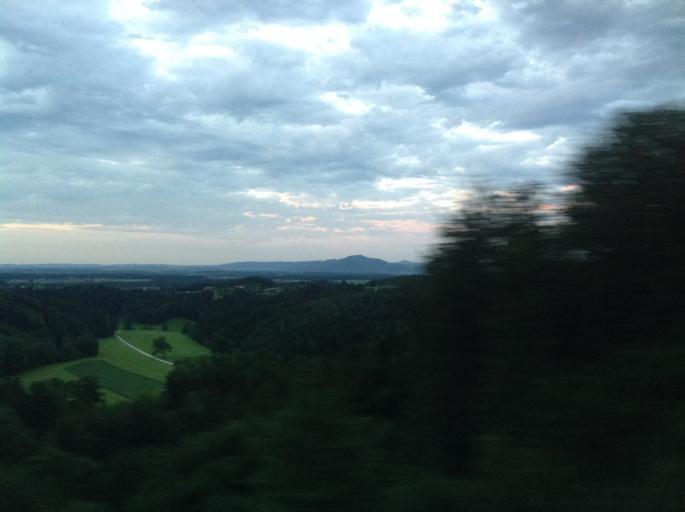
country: DE
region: Bavaria
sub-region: Upper Bavaria
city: Teisendorf
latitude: 47.8220
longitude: 12.8255
